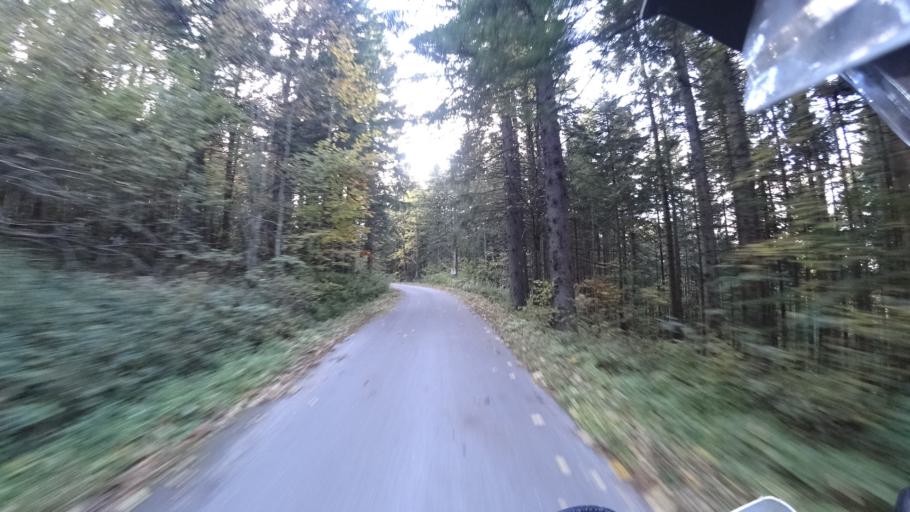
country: HR
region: Karlovacka
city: Plaski
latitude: 44.9800
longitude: 15.4155
